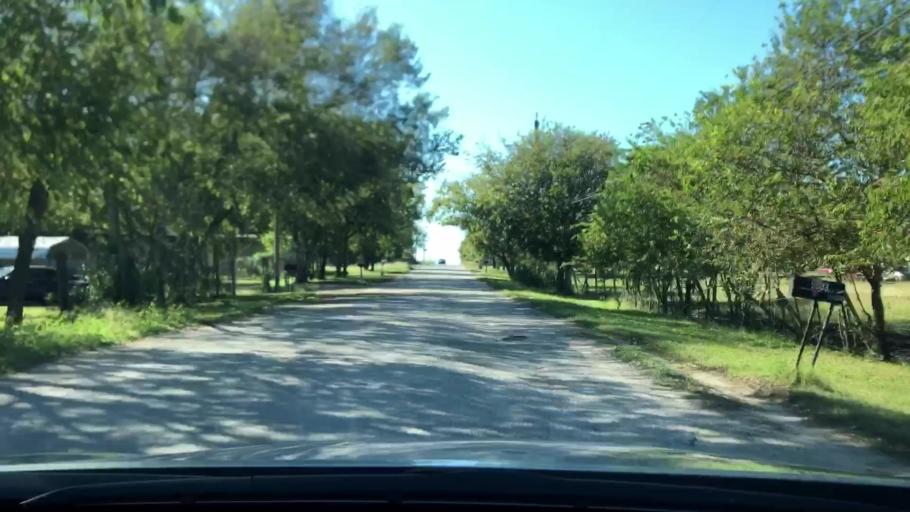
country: US
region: Texas
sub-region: Bexar County
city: Converse
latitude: 29.4684
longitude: -98.3043
